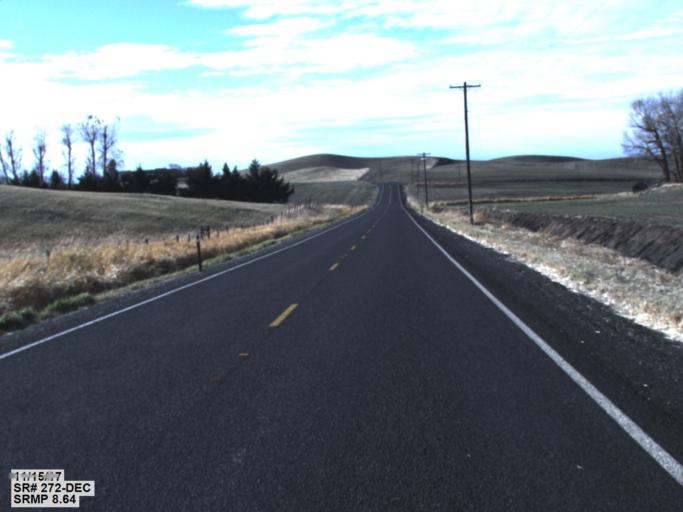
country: US
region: Washington
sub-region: Whitman County
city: Colfax
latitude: 46.9342
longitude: -117.2142
